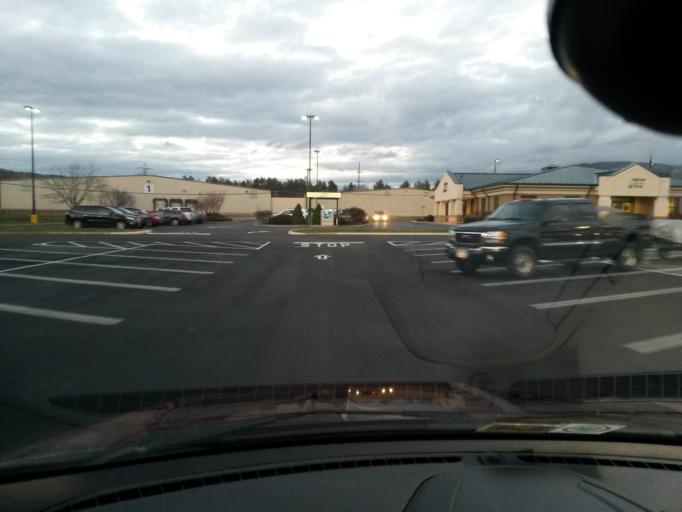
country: US
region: Virginia
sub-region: City of Covington
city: Fairlawn
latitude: 37.7695
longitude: -79.9910
